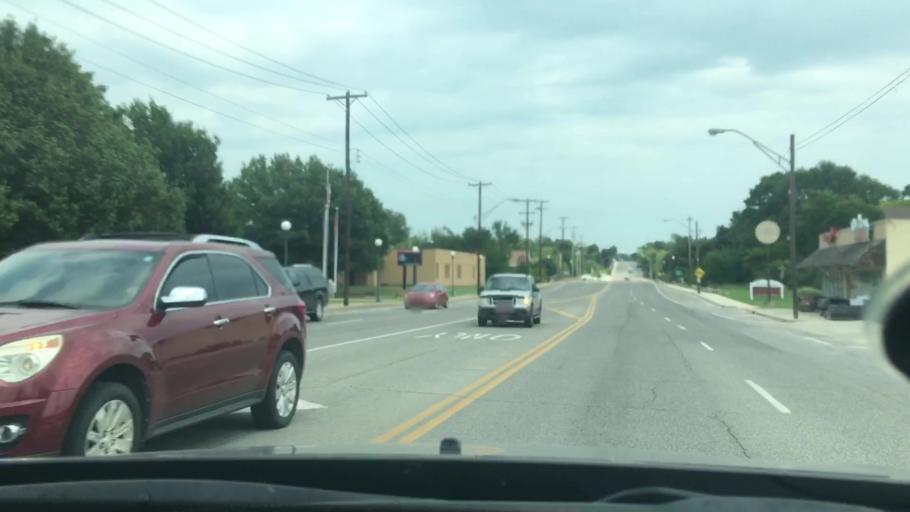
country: US
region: Oklahoma
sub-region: Murray County
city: Sulphur
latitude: 34.5064
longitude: -96.9781
